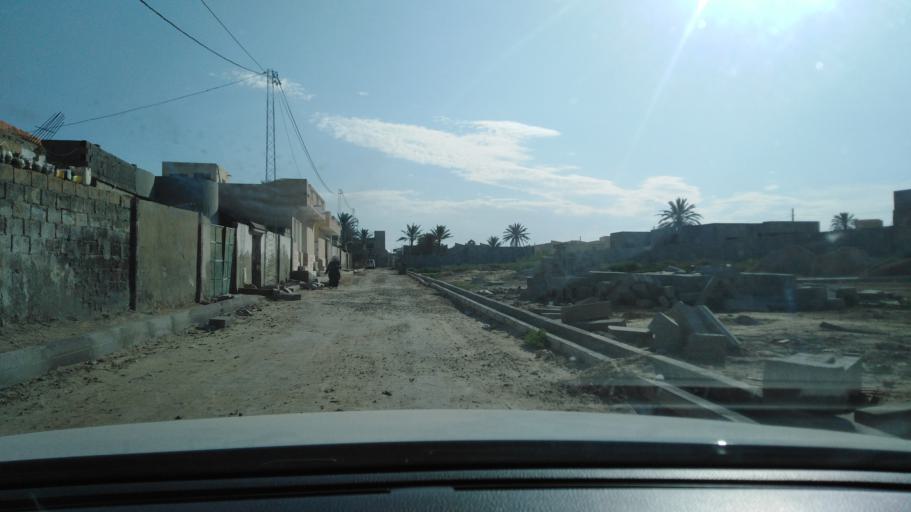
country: TN
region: Qabis
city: Gabes
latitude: 33.9425
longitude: 10.0751
